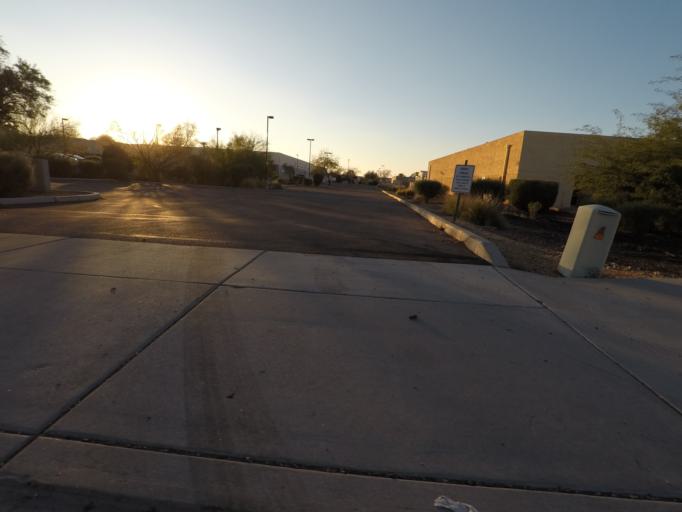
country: US
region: Arizona
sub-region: Maricopa County
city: Tempe Junction
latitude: 33.3940
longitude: -111.9479
